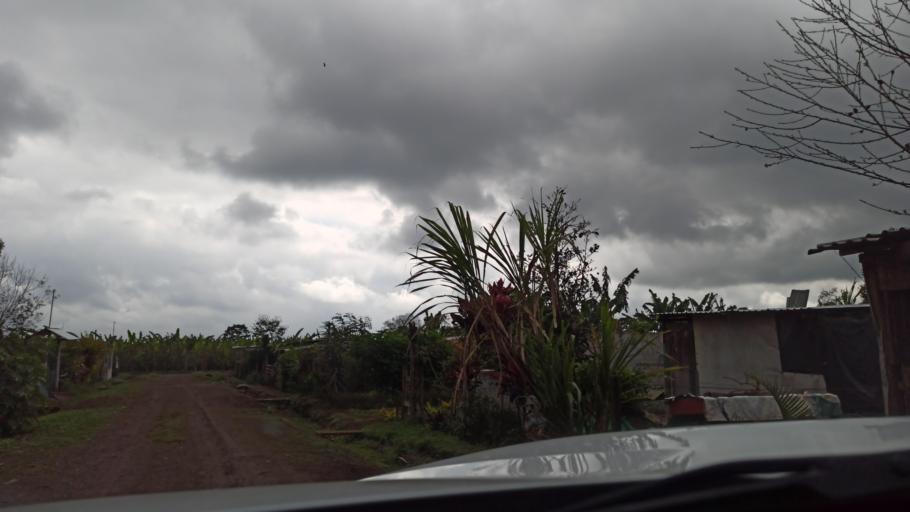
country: MX
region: Veracruz
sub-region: Fortin
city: Santa Lucia Potrerillo
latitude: 18.9672
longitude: -97.0279
